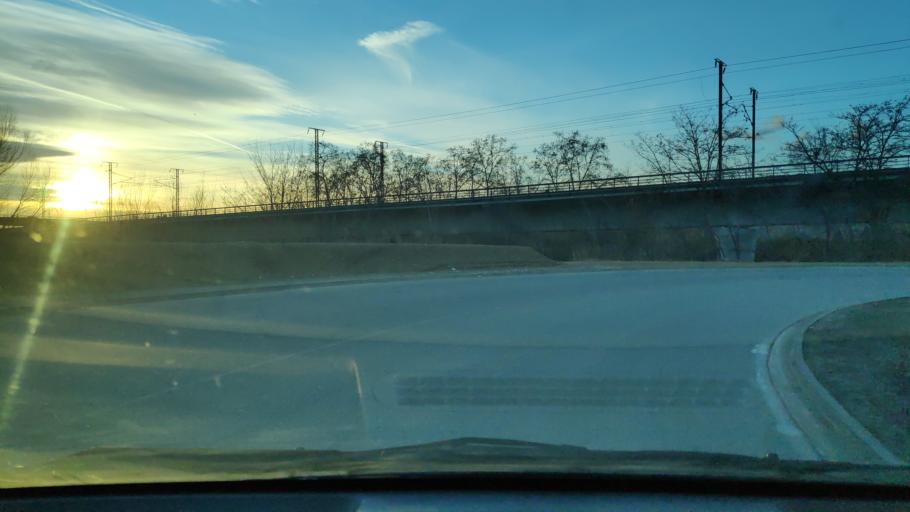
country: ES
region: Catalonia
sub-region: Provincia de Barcelona
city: Montmelo
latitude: 41.5423
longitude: 2.2312
